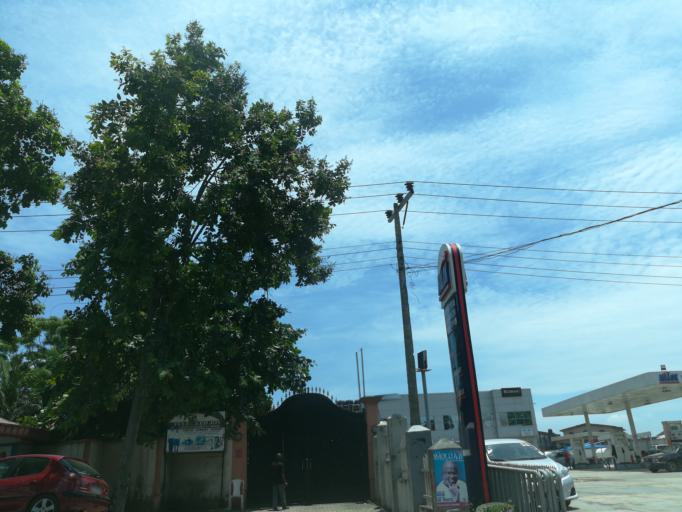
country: NG
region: Lagos
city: Ebute Ikorodu
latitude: 6.6041
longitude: 3.4937
